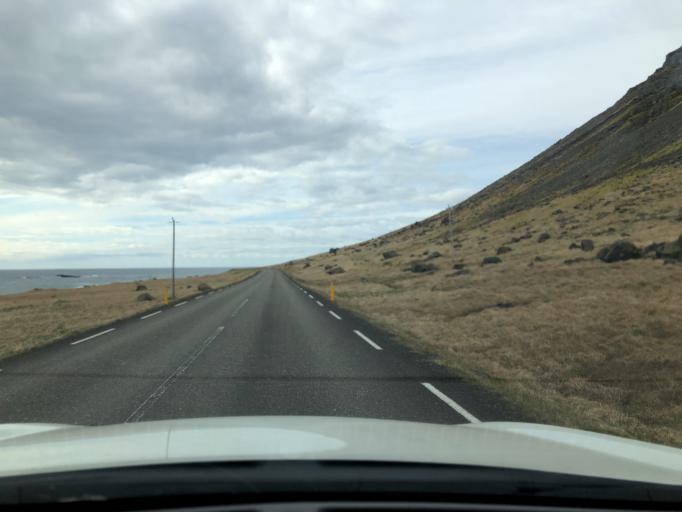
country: IS
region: East
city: Neskaupstadur
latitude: 64.8643
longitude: -13.7612
